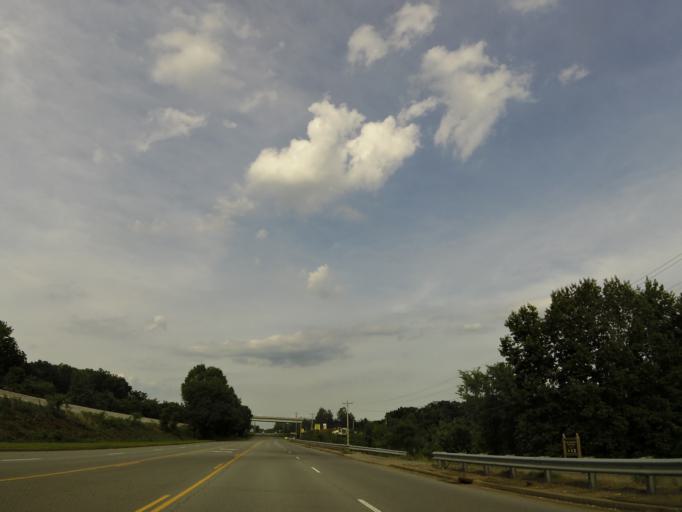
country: US
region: Tennessee
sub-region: Humphreys County
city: New Johnsonville
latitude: 36.0185
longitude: -87.9874
